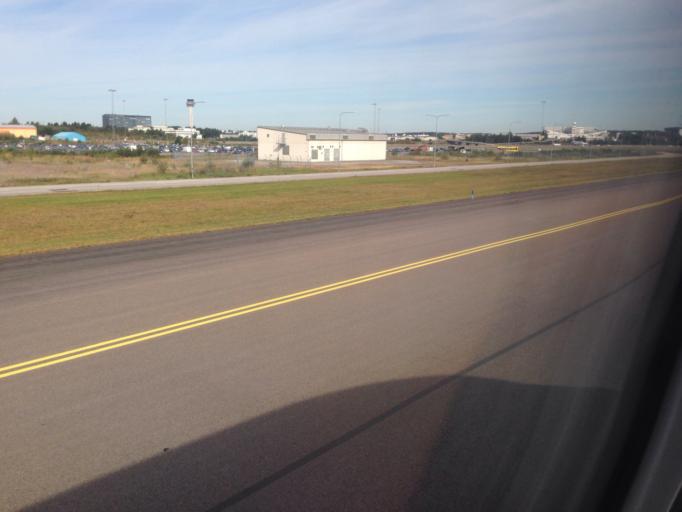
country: SE
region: Stockholm
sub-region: Sigtuna Kommun
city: Rosersberg
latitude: 59.6395
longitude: 17.9515
